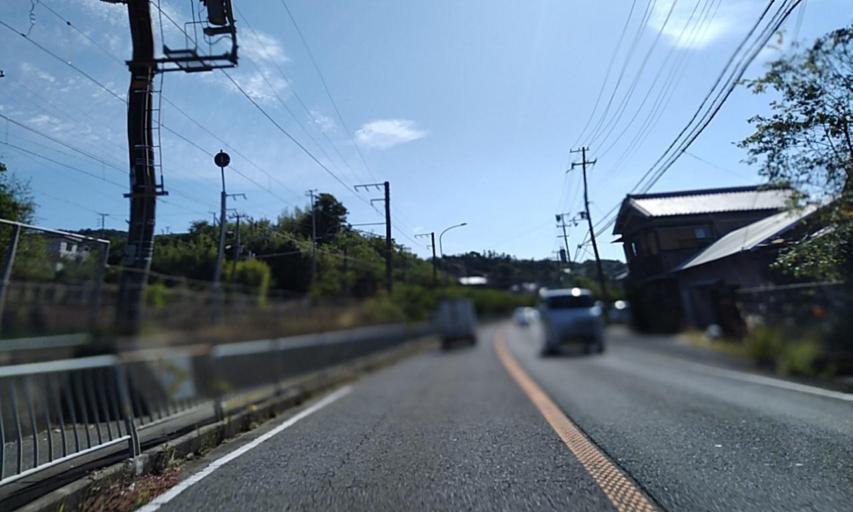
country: JP
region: Wakayama
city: Gobo
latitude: 33.7945
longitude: 135.2406
